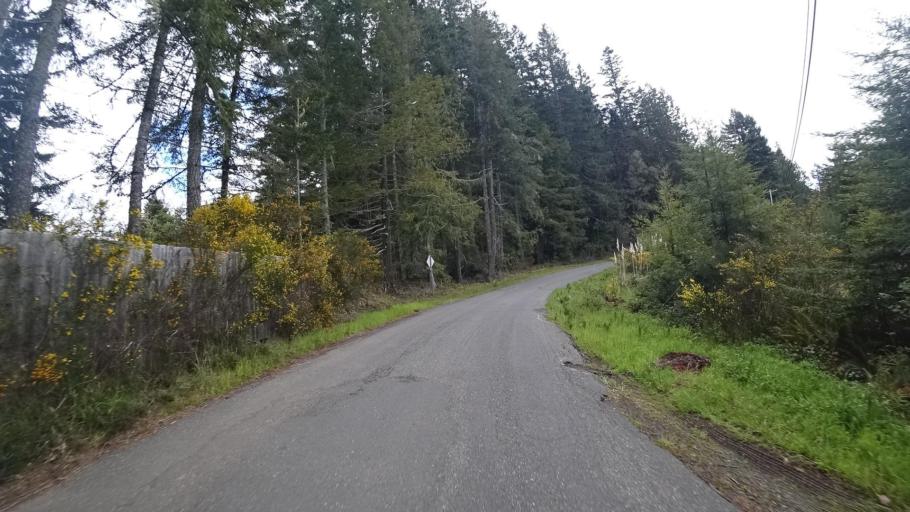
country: US
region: California
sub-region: Humboldt County
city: Blue Lake
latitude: 40.8248
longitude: -124.0014
